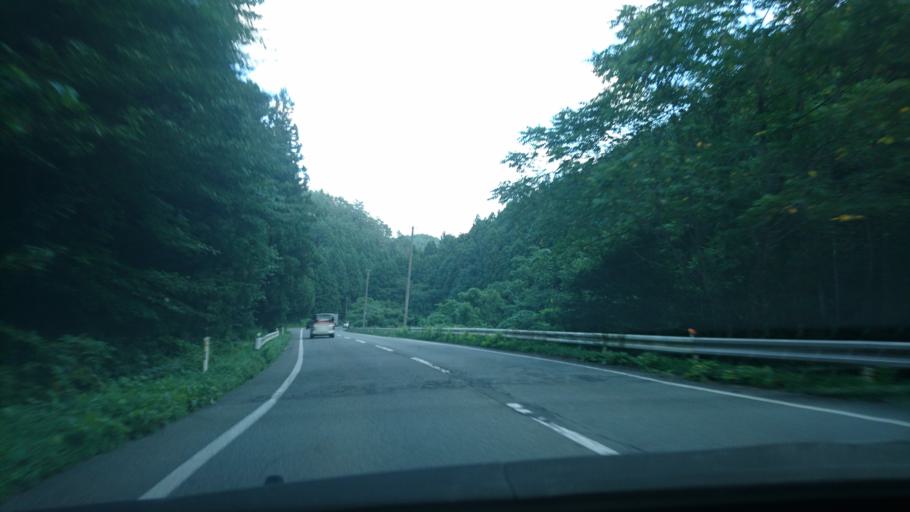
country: JP
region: Iwate
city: Mizusawa
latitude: 39.0459
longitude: 141.2342
